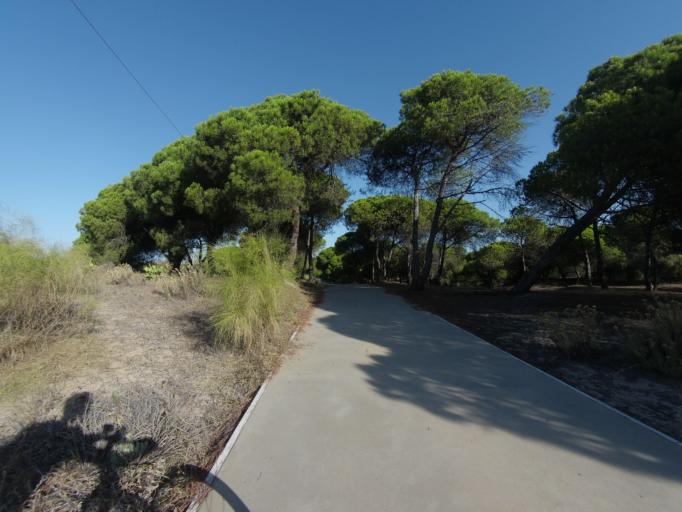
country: ES
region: Andalusia
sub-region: Provincia de Huelva
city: Aljaraque
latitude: 37.2083
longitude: -7.0365
